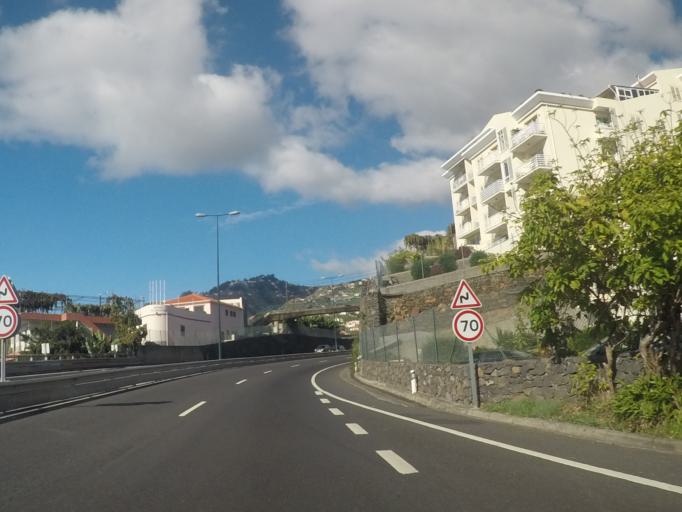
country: PT
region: Madeira
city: Camara de Lobos
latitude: 32.6570
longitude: -16.9744
